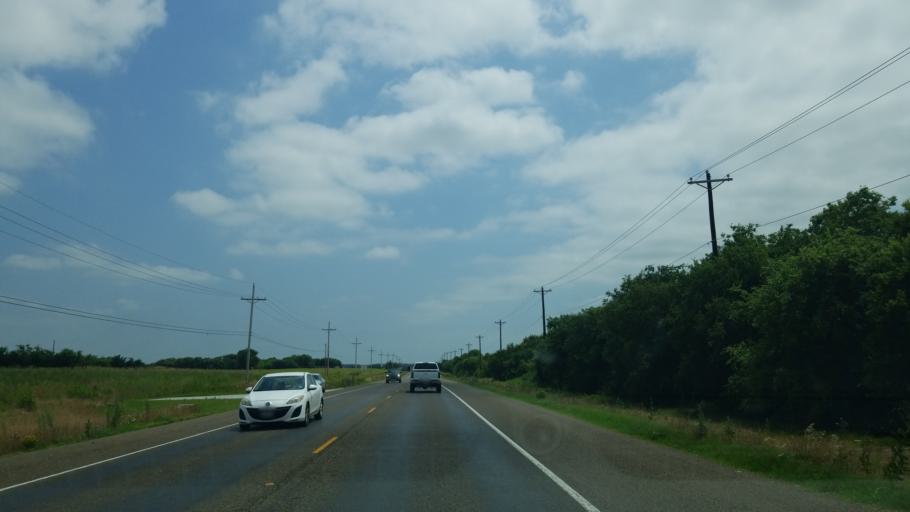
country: US
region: Texas
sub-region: Denton County
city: Pilot Point
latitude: 33.3569
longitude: -96.9664
